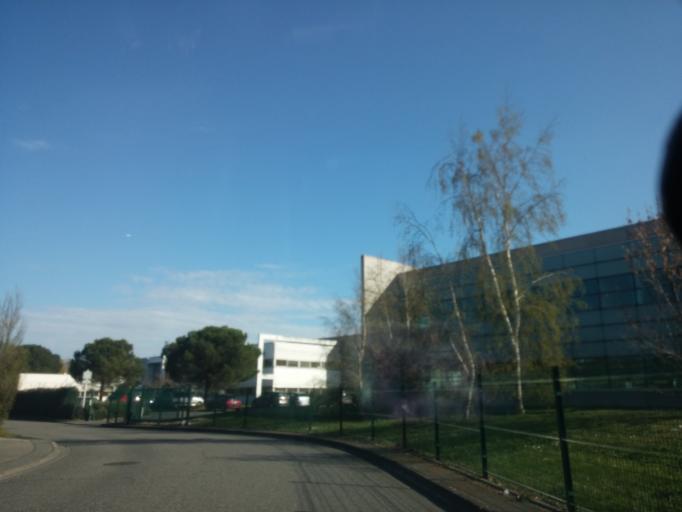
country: FR
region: Midi-Pyrenees
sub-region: Departement de la Haute-Garonne
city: Portet-sur-Garonne
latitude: 43.5681
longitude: 1.3888
